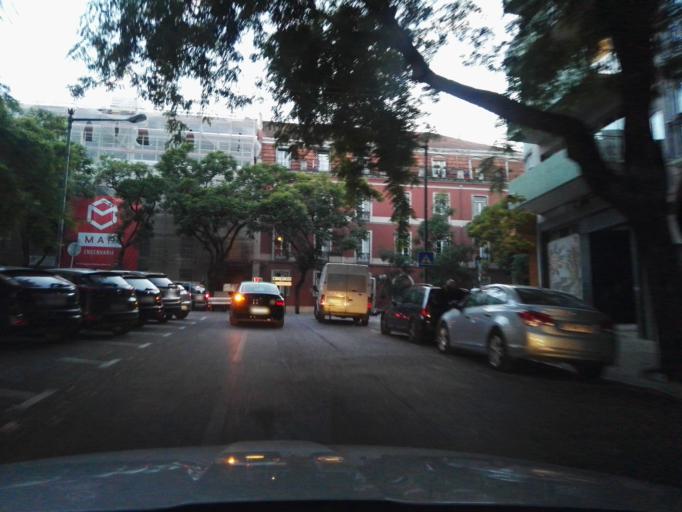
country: PT
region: Lisbon
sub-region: Lisbon
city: Lisbon
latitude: 38.7210
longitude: -9.1508
